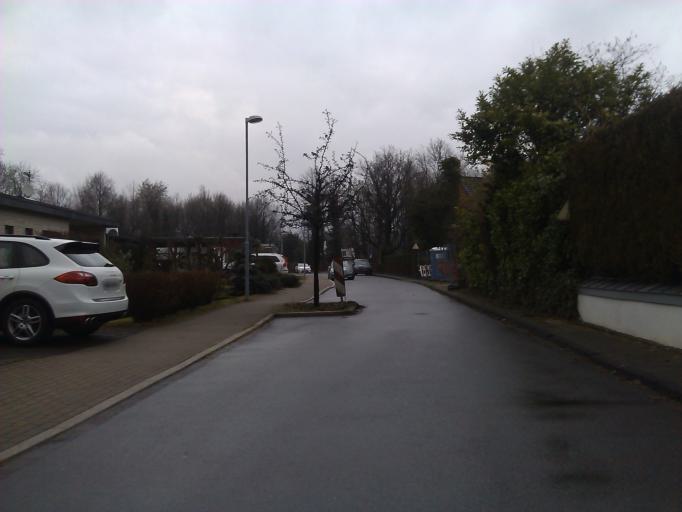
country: DE
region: North Rhine-Westphalia
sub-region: Regierungsbezirk Dusseldorf
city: Heiligenhaus
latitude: 51.3359
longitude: 6.9166
